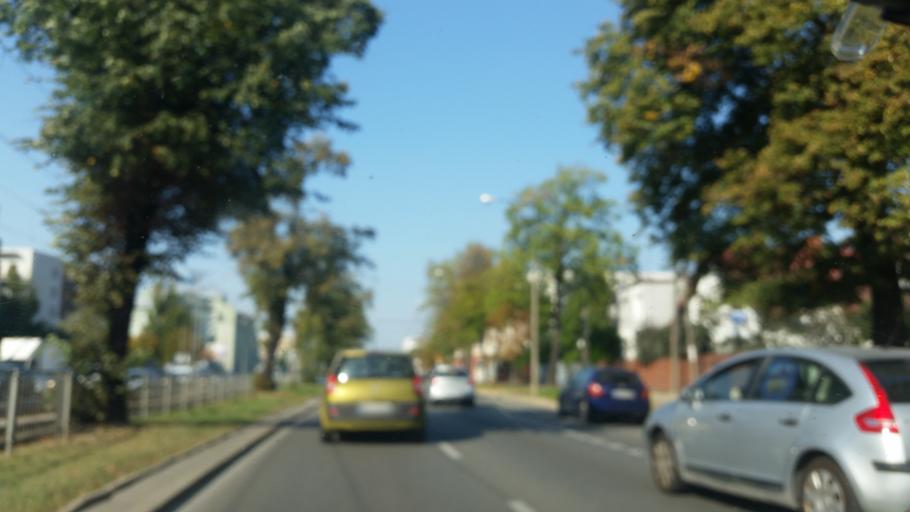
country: PL
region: Masovian Voivodeship
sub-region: Warszawa
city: Bemowo
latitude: 52.2301
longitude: 20.9152
